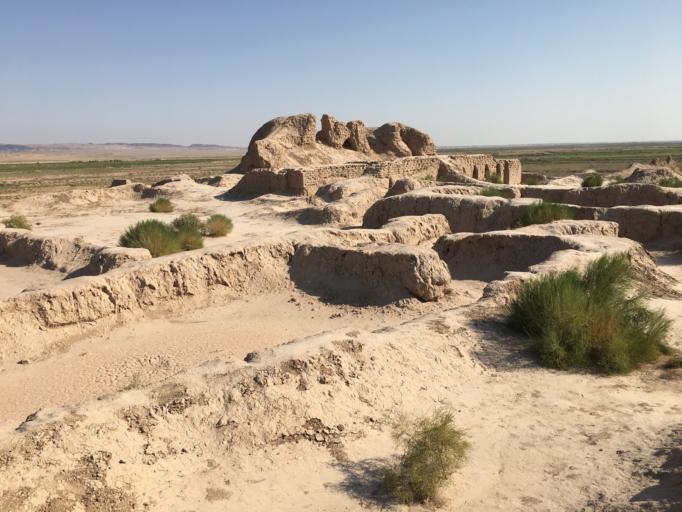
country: UZ
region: Karakalpakstan
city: Bo'ston Shahri
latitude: 41.9283
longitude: 60.8207
